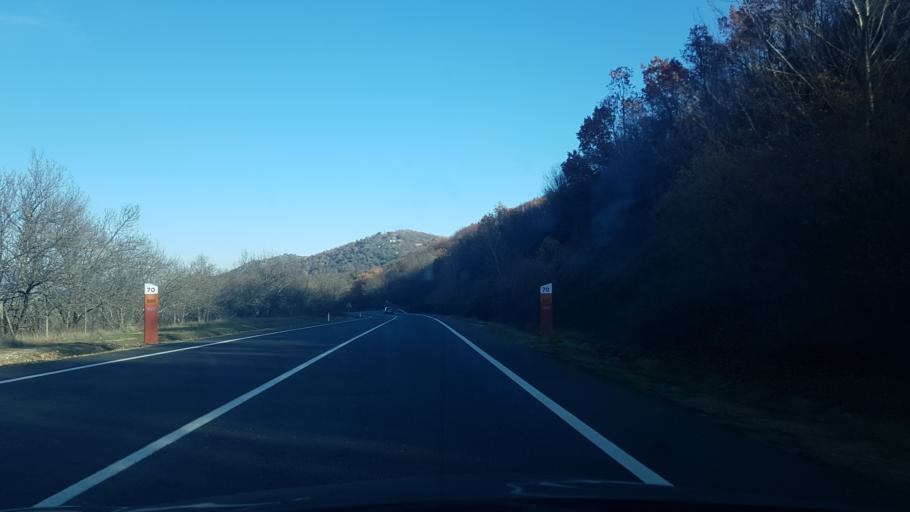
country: ES
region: Castille and Leon
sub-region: Provincia de Avila
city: Navahondilla
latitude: 40.3107
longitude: -4.5146
